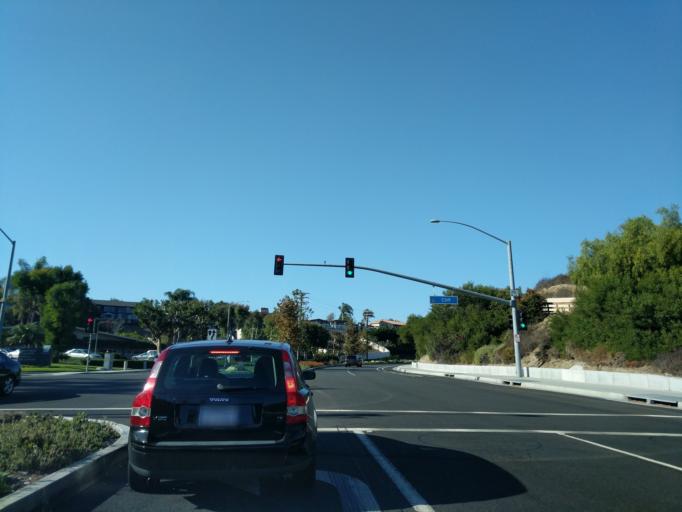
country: US
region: California
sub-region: Orange County
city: Newport Beach
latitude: 33.6188
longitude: -117.9073
